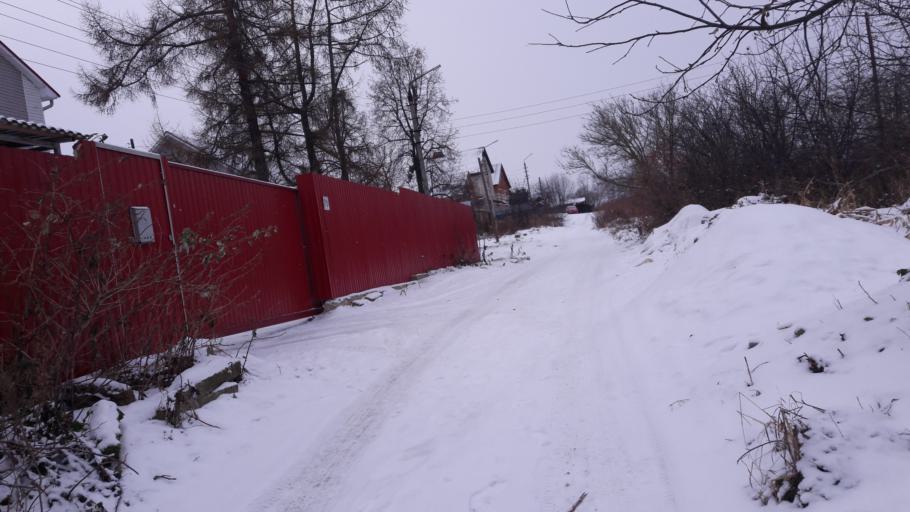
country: RU
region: Tula
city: Gorelki
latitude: 54.2365
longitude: 37.6342
